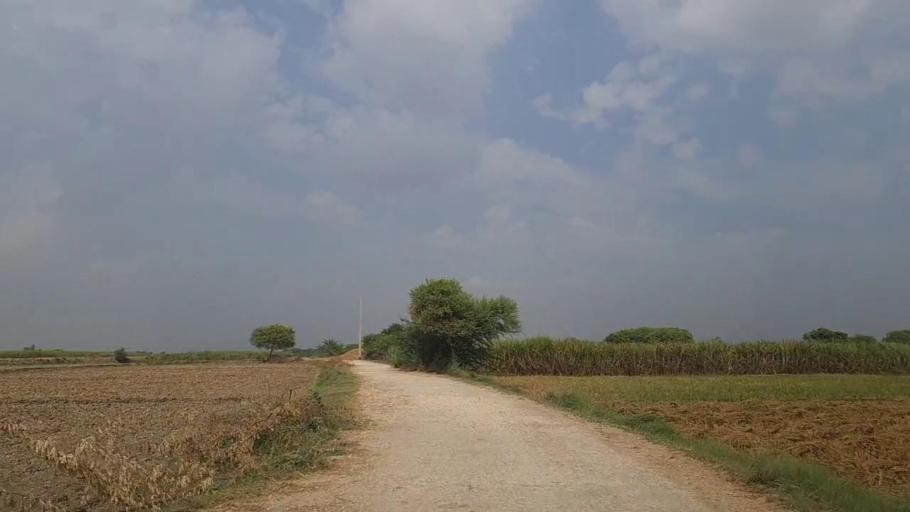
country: PK
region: Sindh
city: Daro Mehar
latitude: 24.6908
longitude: 68.1264
